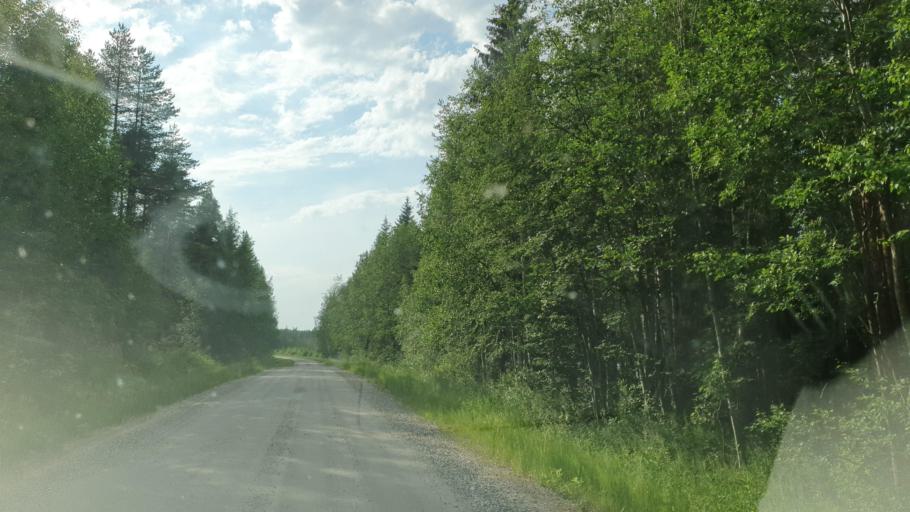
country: FI
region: Kainuu
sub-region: Kehys-Kainuu
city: Kuhmo
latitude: 64.0781
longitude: 29.7105
